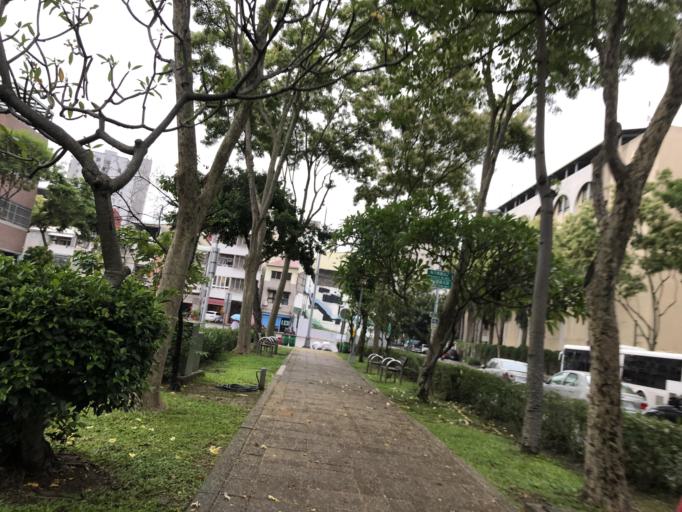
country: TW
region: Taiwan
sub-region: Taichung City
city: Taichung
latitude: 24.1541
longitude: 120.6742
